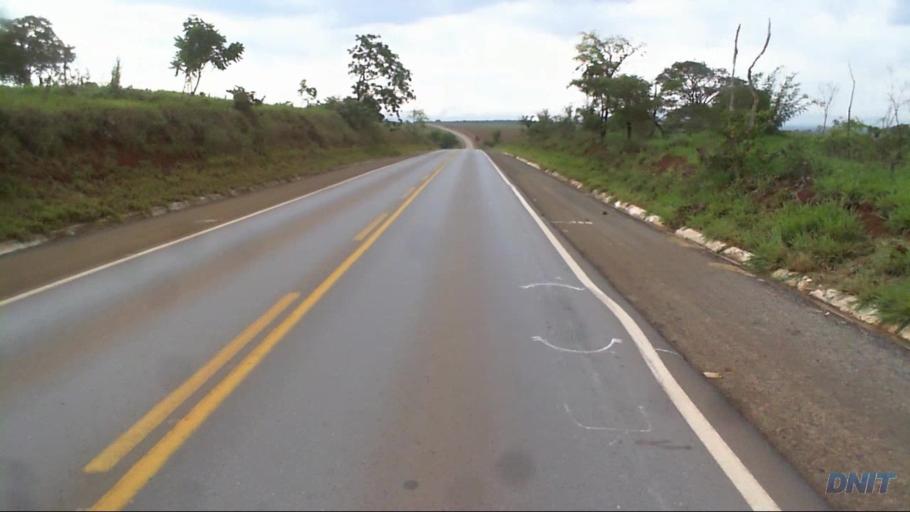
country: BR
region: Goias
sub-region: Uruacu
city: Uruacu
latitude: -14.6843
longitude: -49.1330
